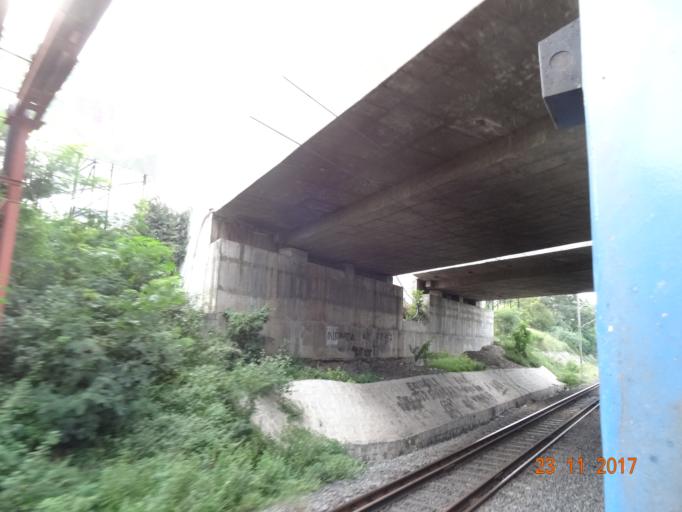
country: IN
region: Tamil Nadu
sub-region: Coimbatore
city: Singanallur
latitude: 11.0262
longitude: 77.0216
